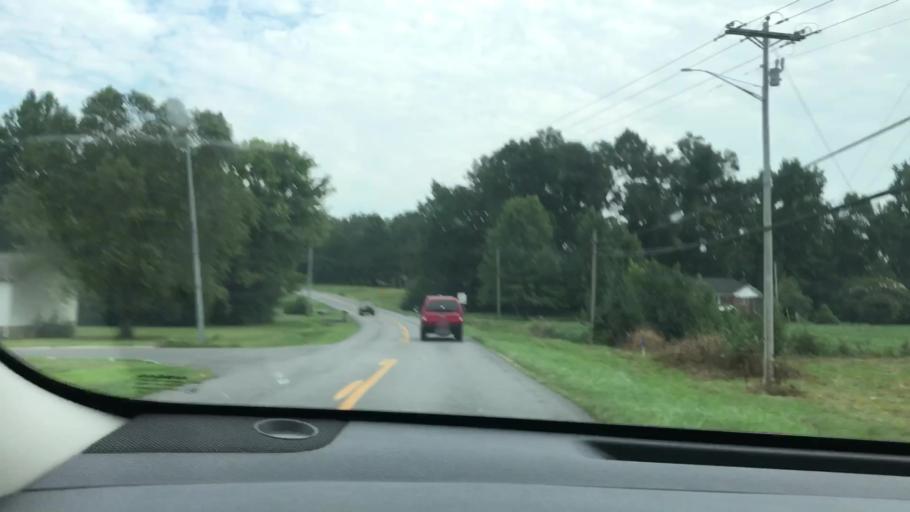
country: US
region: Kentucky
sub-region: Calloway County
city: Murray
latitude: 36.6285
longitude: -88.3019
